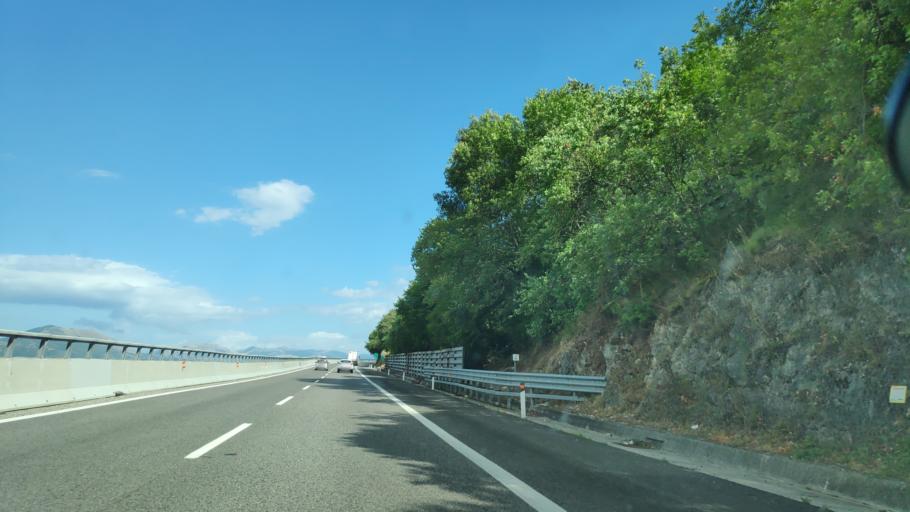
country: IT
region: Campania
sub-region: Provincia di Salerno
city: Sicignano degli Alburni
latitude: 40.5913
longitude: 15.3286
